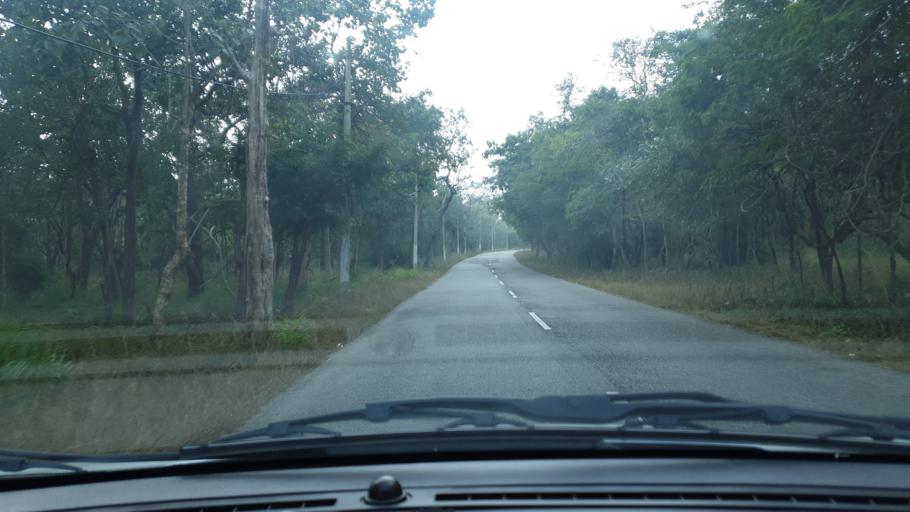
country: IN
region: Andhra Pradesh
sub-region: Kurnool
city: Srisailam
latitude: 16.2928
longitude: 78.7307
